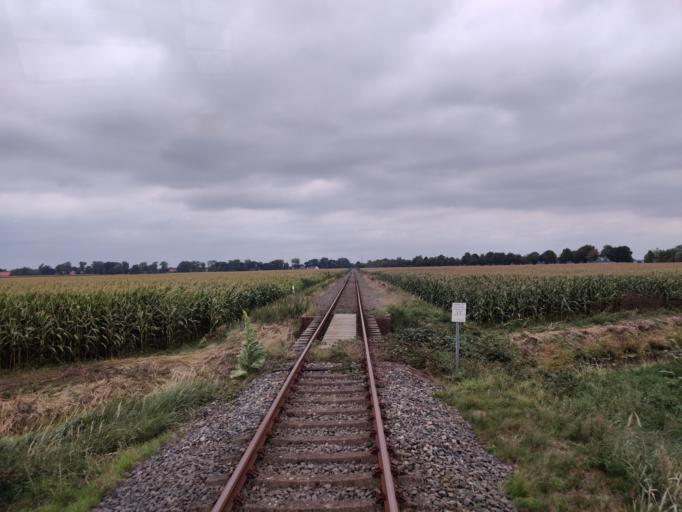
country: DE
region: Lower Saxony
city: Vollersode
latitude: 53.3020
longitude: 8.9707
